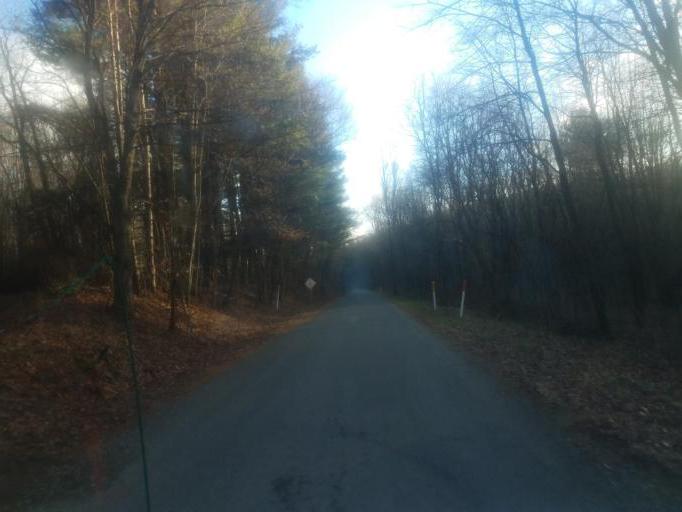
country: US
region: Ohio
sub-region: Sandusky County
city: Bellville
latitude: 40.6021
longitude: -82.3954
